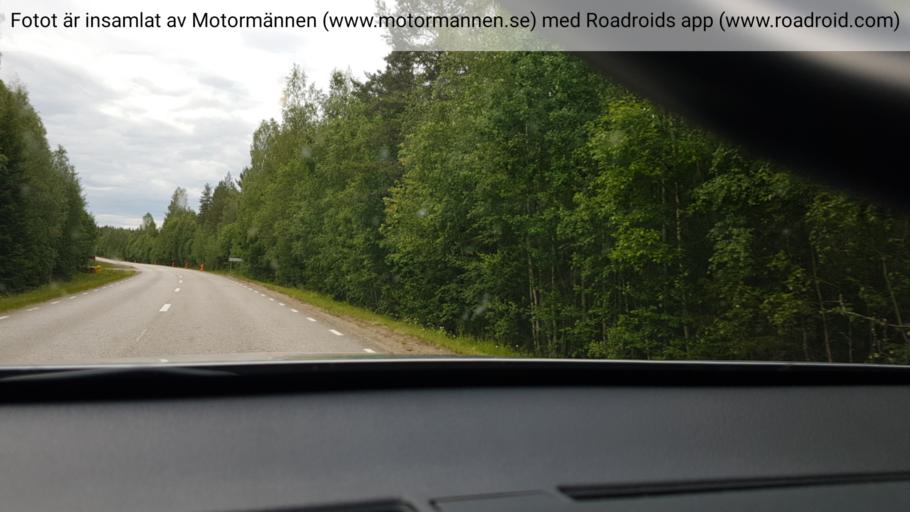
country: NO
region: Hedmark
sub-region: Trysil
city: Innbygda
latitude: 60.9102
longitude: 12.5544
